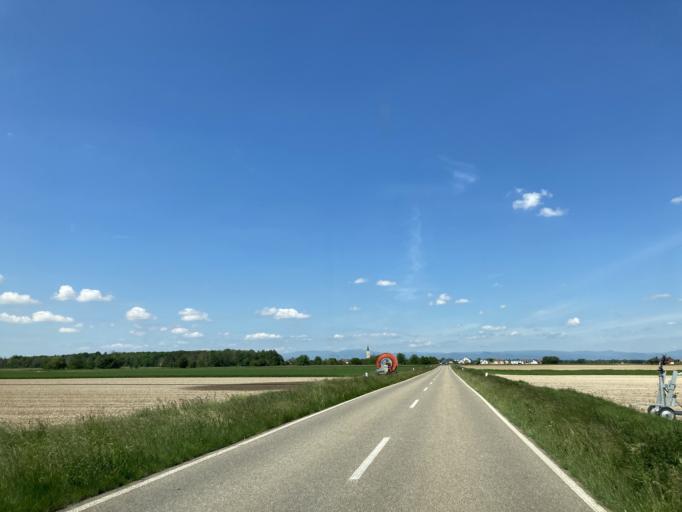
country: DE
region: Baden-Wuerttemberg
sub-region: Freiburg Region
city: Hartheim
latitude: 47.9146
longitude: 7.6407
